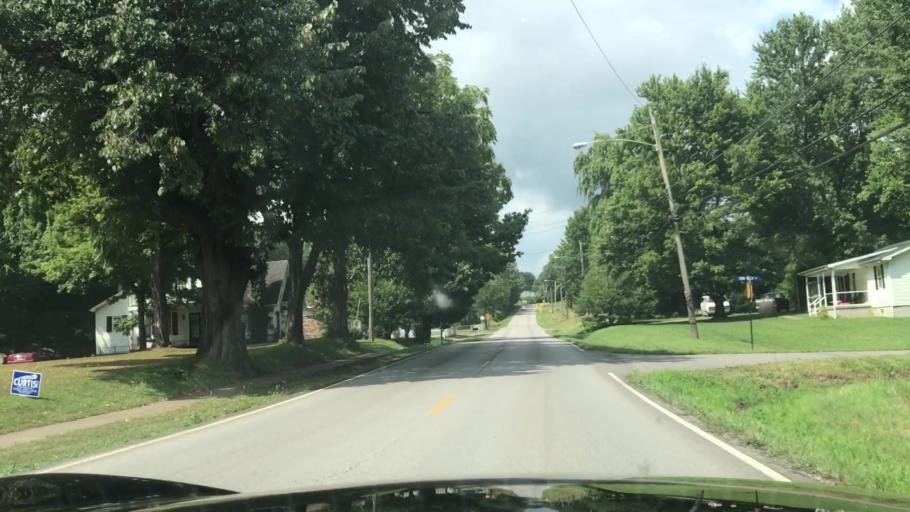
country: US
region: Kentucky
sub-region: Muhlenberg County
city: Central City
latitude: 37.2156
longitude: -87.0535
